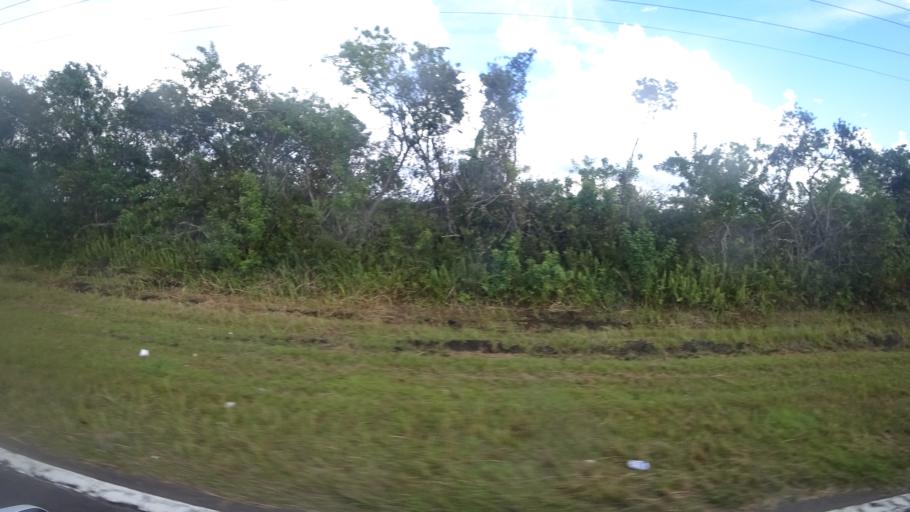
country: US
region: Florida
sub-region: Hillsborough County
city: Ruskin
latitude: 27.6507
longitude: -82.4293
